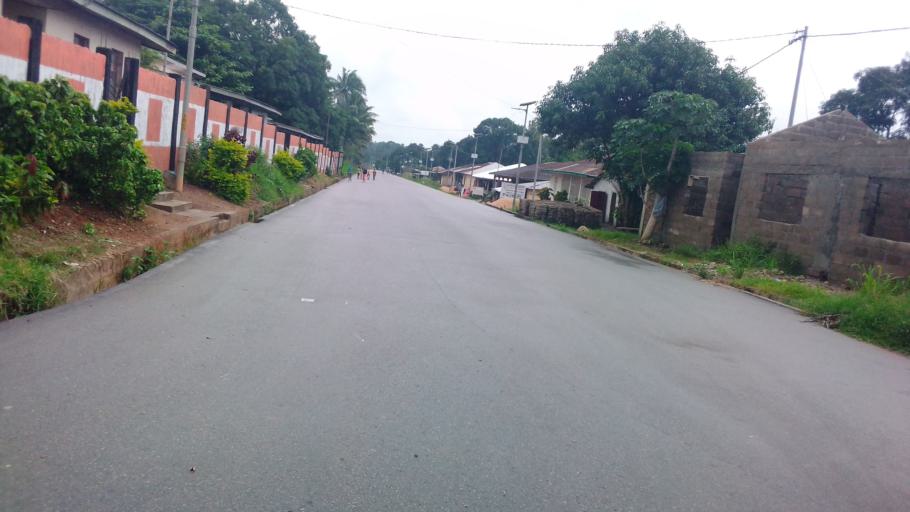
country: SL
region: Northern Province
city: Lunsar
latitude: 8.6843
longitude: -12.5348
